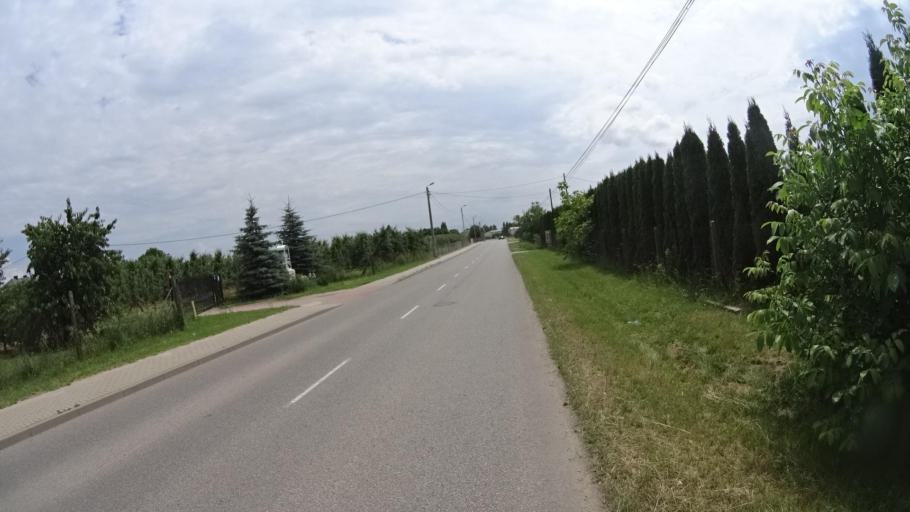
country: PL
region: Masovian Voivodeship
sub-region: Powiat piaseczynski
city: Tarczyn
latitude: 51.9935
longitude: 20.8197
